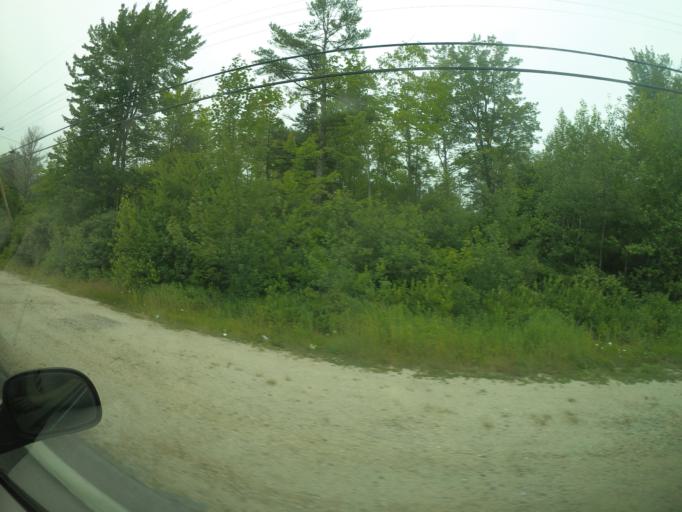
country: US
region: Maine
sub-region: York County
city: Arundel
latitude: 43.4007
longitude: -70.4865
